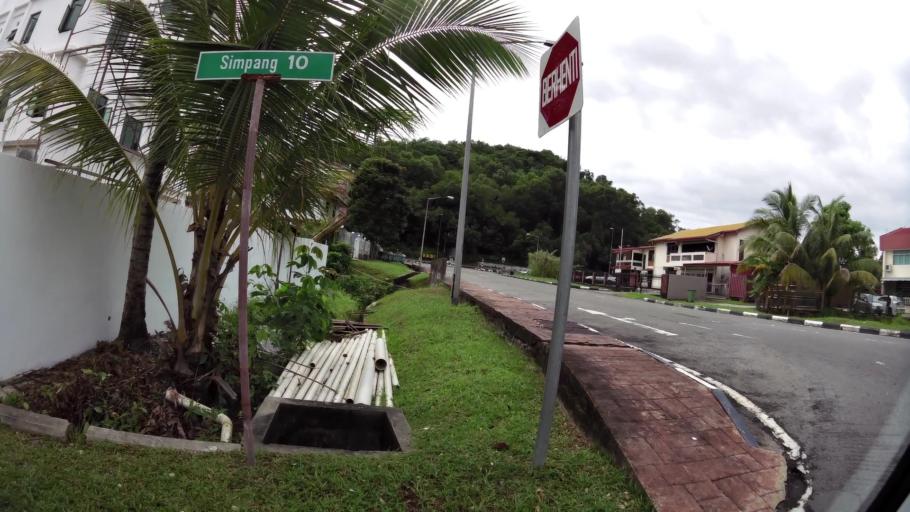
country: BN
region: Brunei and Muara
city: Bandar Seri Begawan
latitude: 4.9059
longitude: 114.9399
